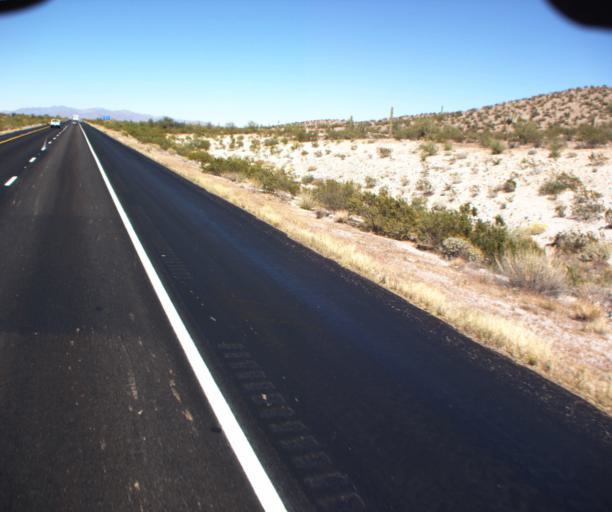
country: US
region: Arizona
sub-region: Maricopa County
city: Buckeye
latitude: 33.2534
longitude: -112.6363
